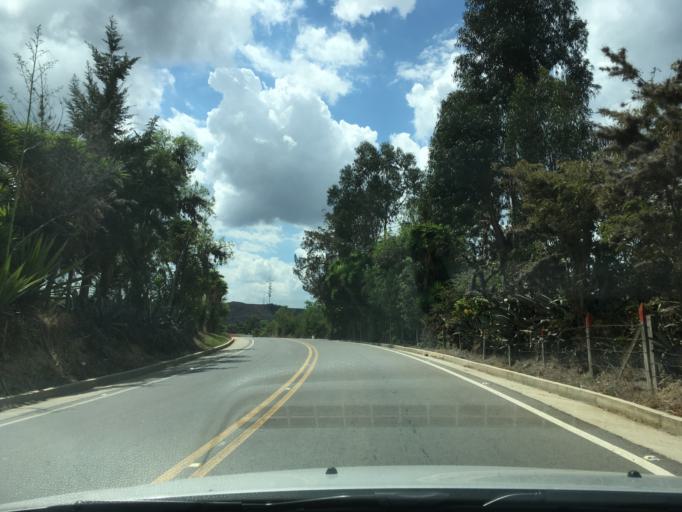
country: CO
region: Boyaca
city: Sutamarchan
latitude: 5.6196
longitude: -73.6102
